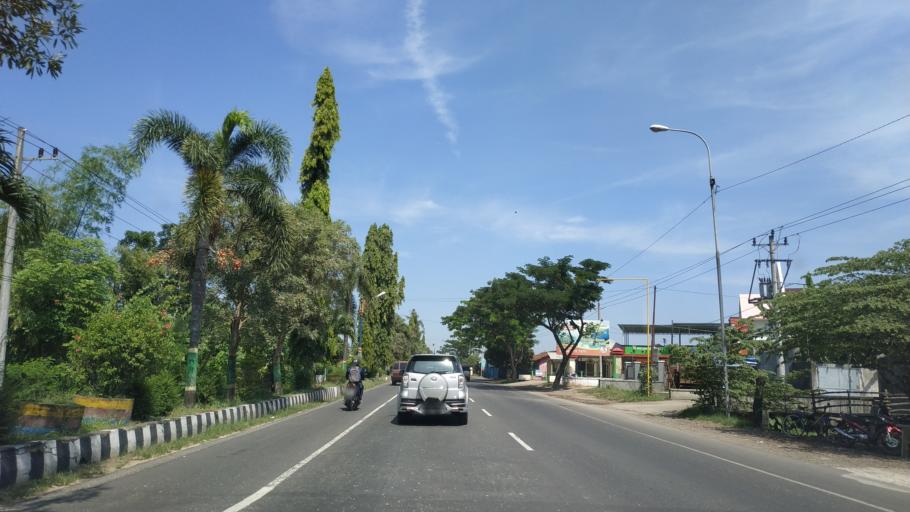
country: ID
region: Central Java
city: Geritan
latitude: -6.7489
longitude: 111.0600
